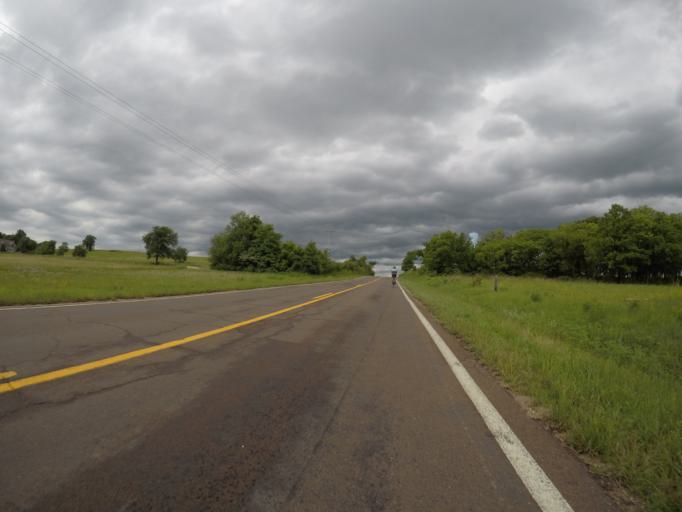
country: US
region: Kansas
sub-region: Shawnee County
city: Auburn
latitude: 38.9645
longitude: -95.9217
